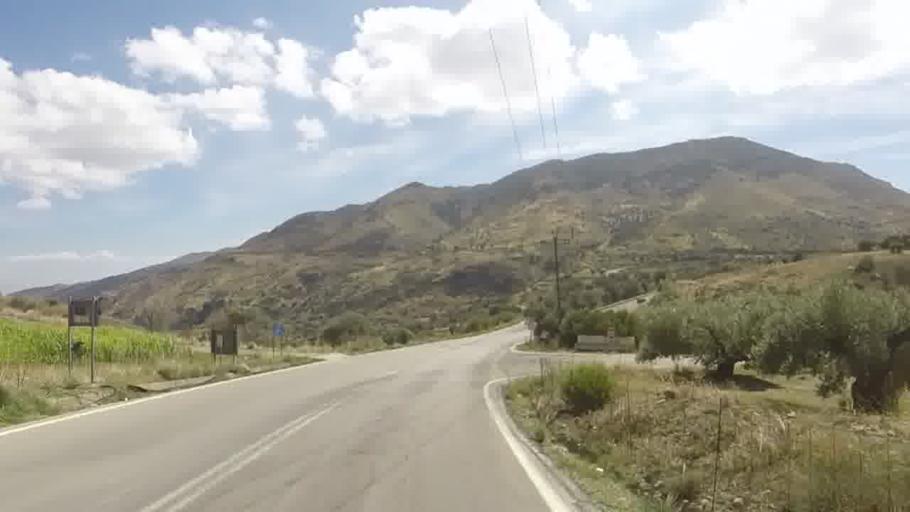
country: GR
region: Crete
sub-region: Nomos Rethymnis
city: Agia Galini
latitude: 35.1473
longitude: 24.6334
